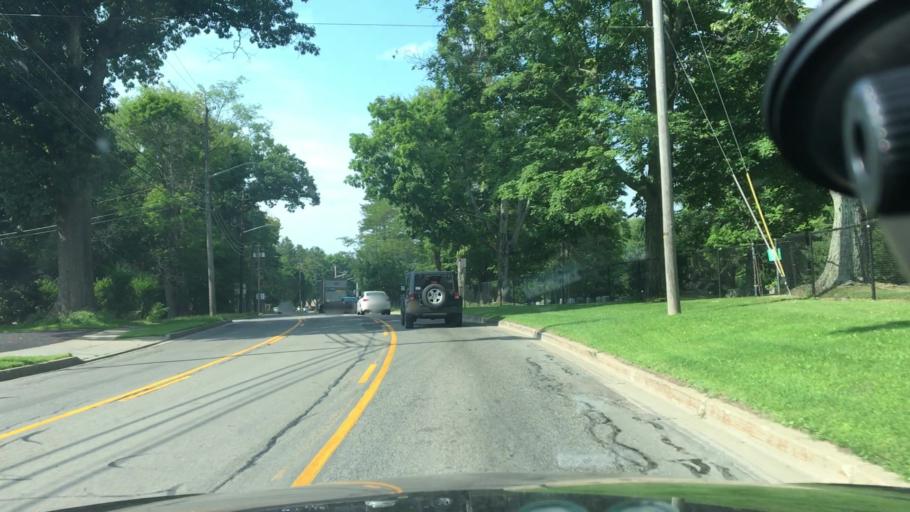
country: US
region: New York
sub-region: Chautauqua County
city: Jamestown
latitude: 42.1145
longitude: -79.2406
